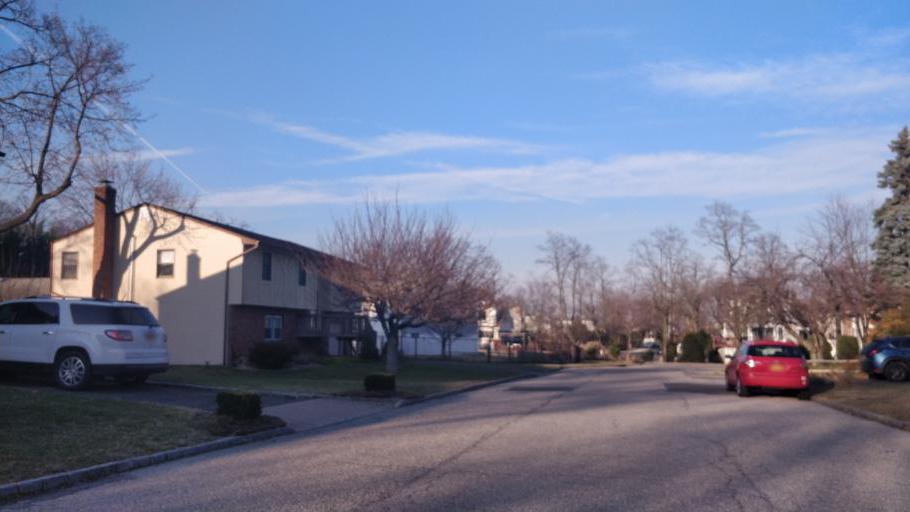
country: US
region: New York
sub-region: Nassau County
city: Bayville
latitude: 40.9073
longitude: -73.5575
